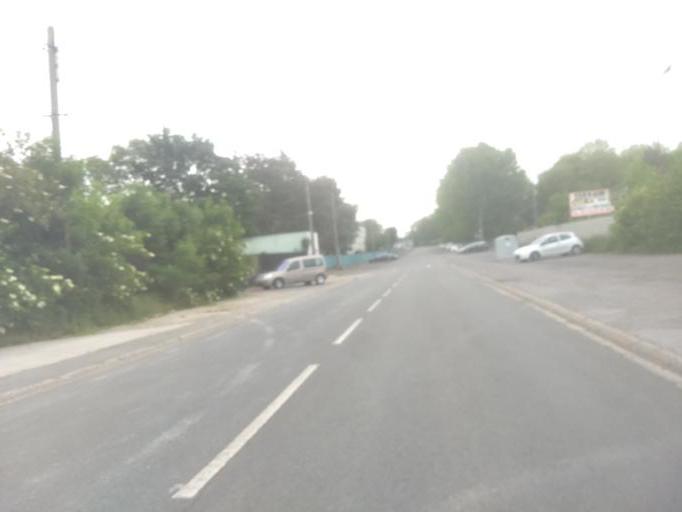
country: FR
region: Nord-Pas-de-Calais
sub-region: Departement du Pas-de-Calais
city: Dainville
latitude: 50.2974
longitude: 2.7327
